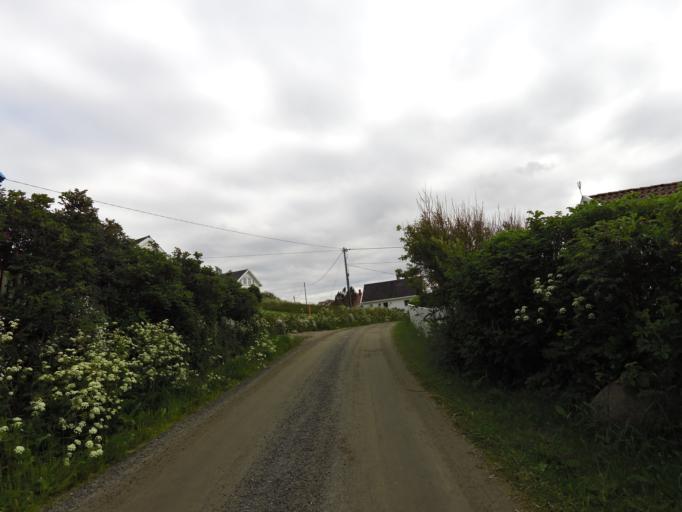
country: NO
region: Vest-Agder
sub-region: Farsund
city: Vestbygd
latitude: 58.1399
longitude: 6.6101
